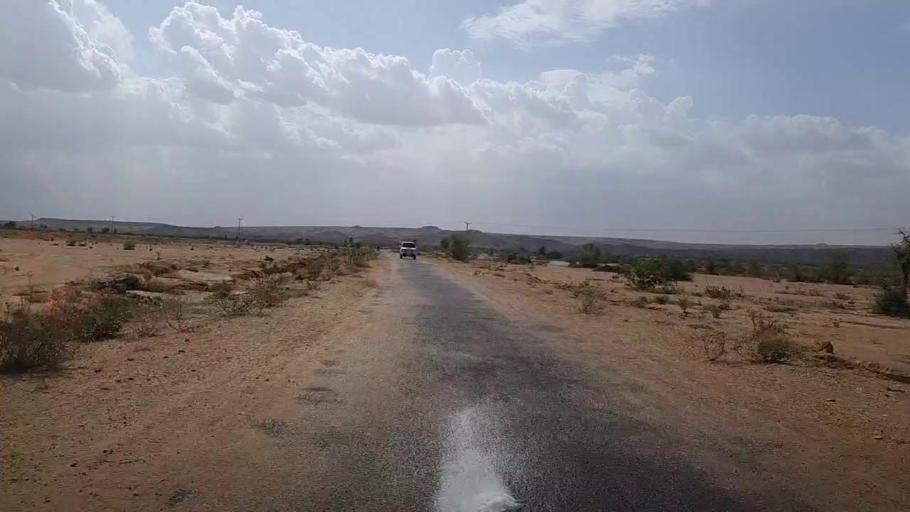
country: PK
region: Sindh
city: Jamshoro
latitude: 25.4030
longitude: 67.7728
